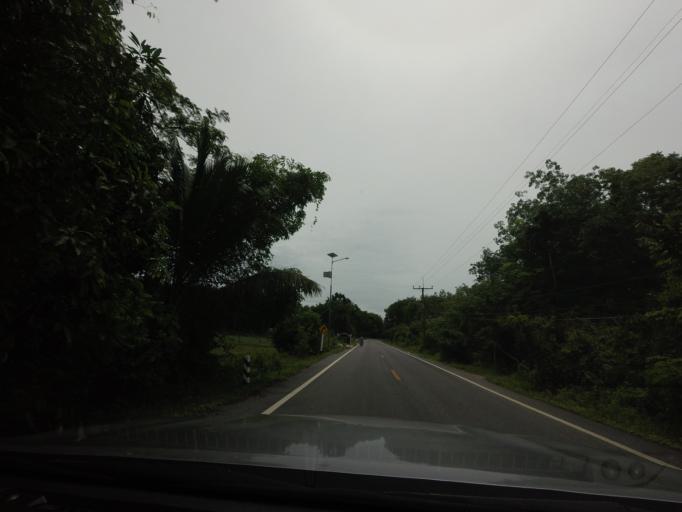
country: TH
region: Pattani
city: Kapho
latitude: 6.6231
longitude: 101.5445
